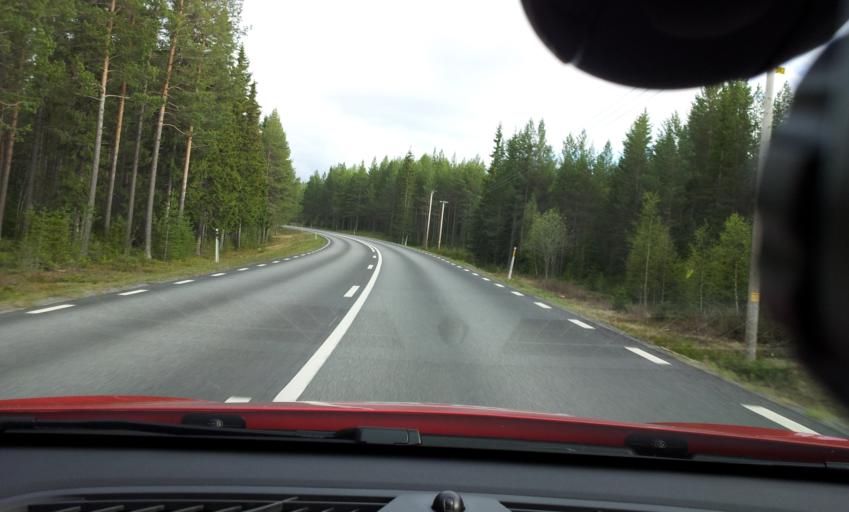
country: SE
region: Jaemtland
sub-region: Krokoms Kommun
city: Krokom
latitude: 63.2073
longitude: 14.4734
